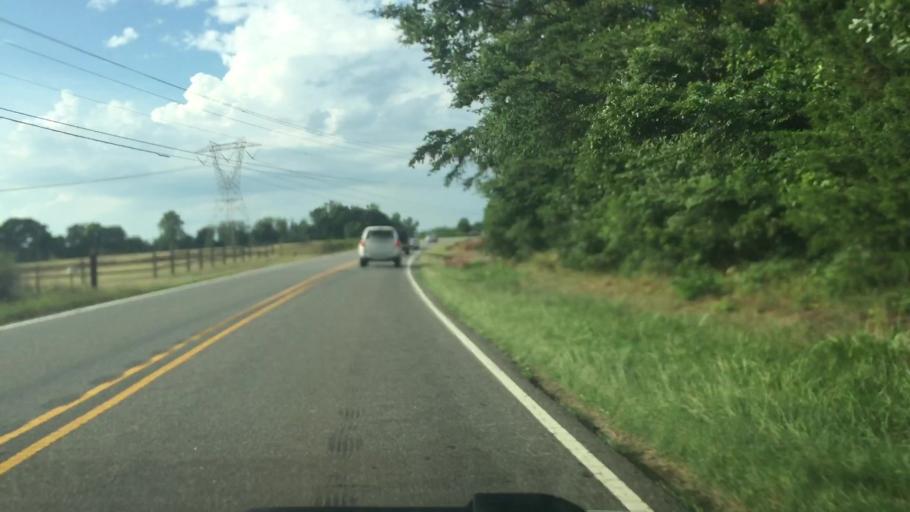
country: US
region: North Carolina
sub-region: Iredell County
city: Mooresville
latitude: 35.5347
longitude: -80.7692
